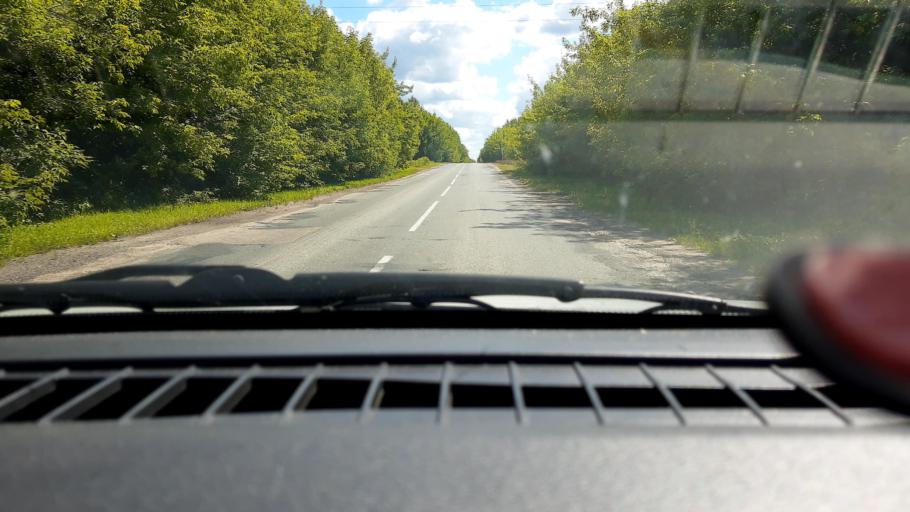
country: RU
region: Nizjnij Novgorod
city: Kstovo
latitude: 56.1330
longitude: 44.0986
